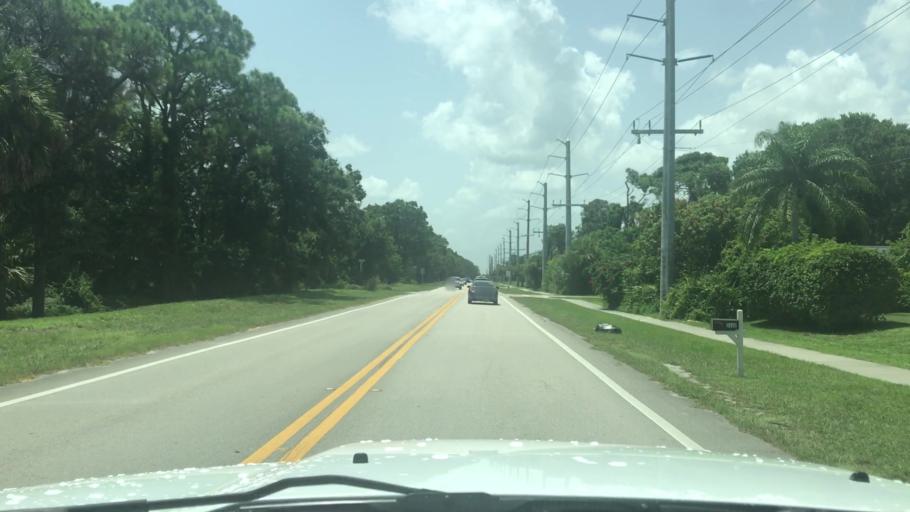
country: US
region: Florida
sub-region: Indian River County
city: Vero Beach South
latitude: 27.6238
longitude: -80.4218
